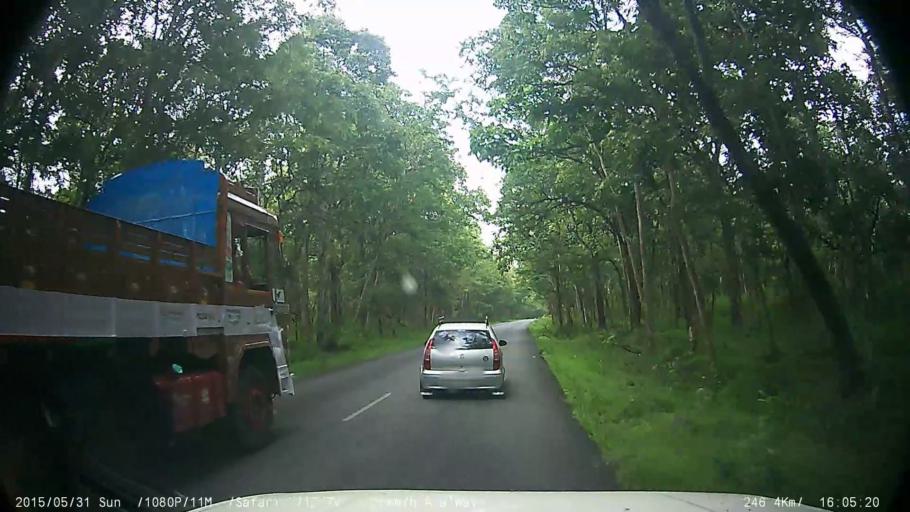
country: IN
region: Tamil Nadu
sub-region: Nilgiri
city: Masinigudi
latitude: 11.7130
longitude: 76.4190
